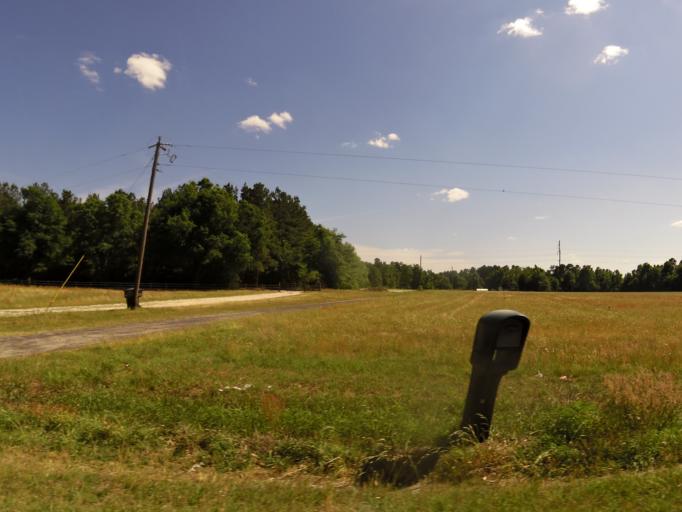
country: US
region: South Carolina
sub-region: Barnwell County
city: Williston
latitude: 33.4134
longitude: -81.4647
